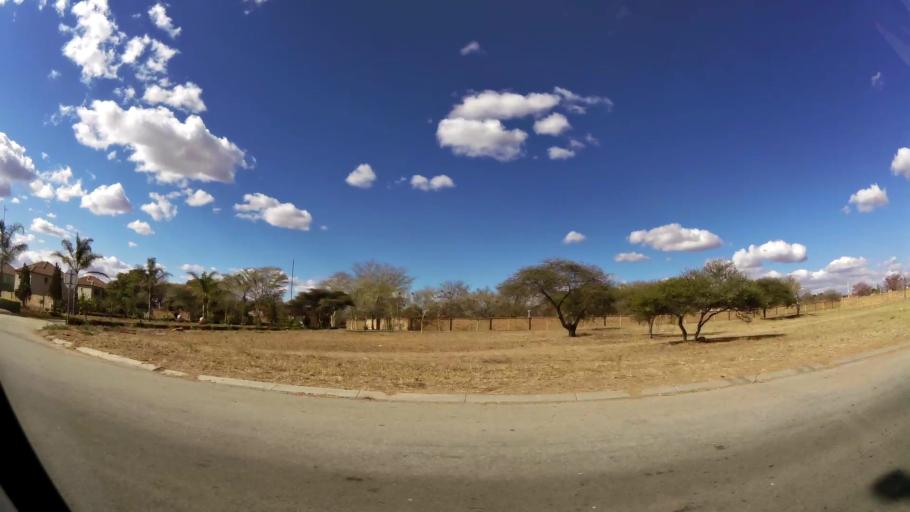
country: ZA
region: Limpopo
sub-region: Capricorn District Municipality
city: Polokwane
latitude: -23.8853
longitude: 29.4745
